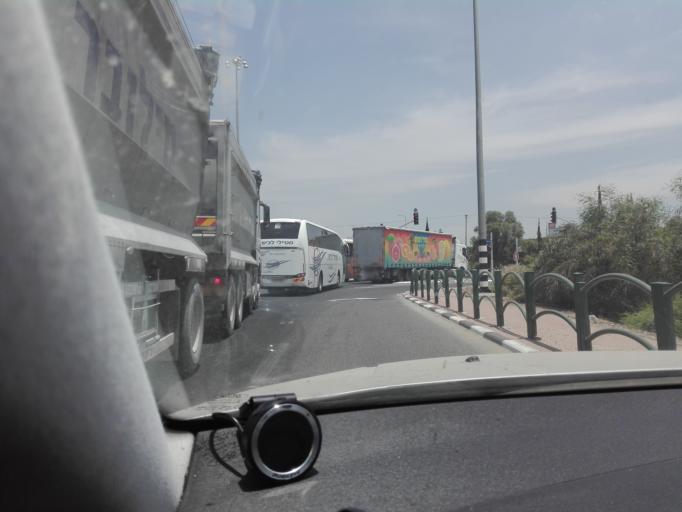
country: IL
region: Central District
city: Bene 'Ayish
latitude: 31.7326
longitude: 34.7572
